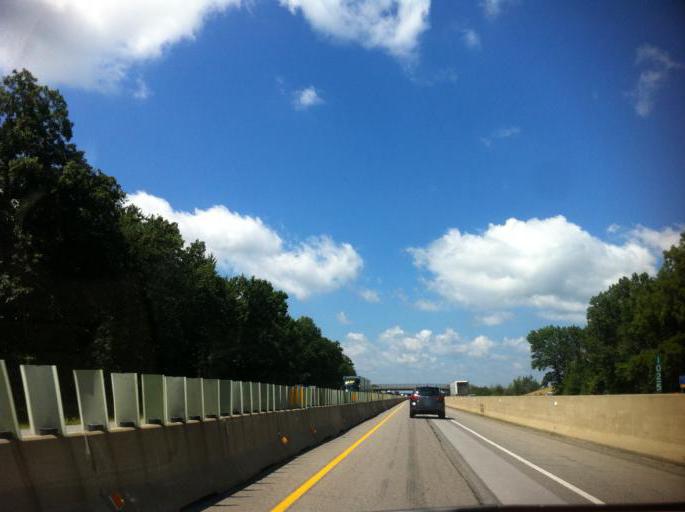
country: US
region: Ohio
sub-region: Sandusky County
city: Clyde
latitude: 41.3596
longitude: -82.9108
